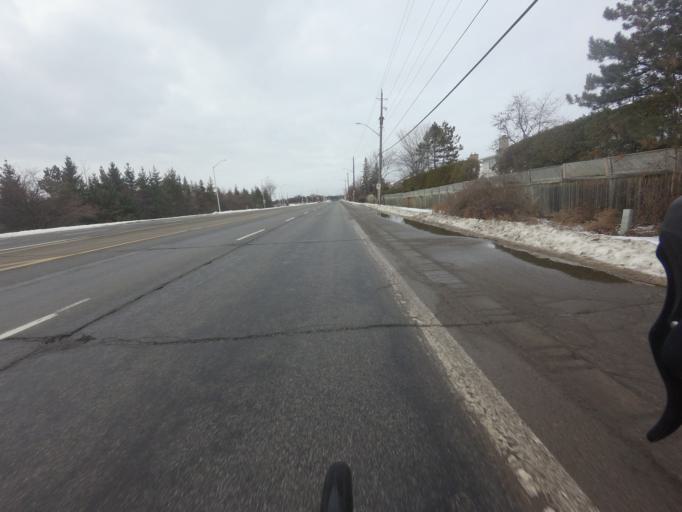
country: CA
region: Ontario
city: Bells Corners
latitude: 45.3528
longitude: -75.8438
